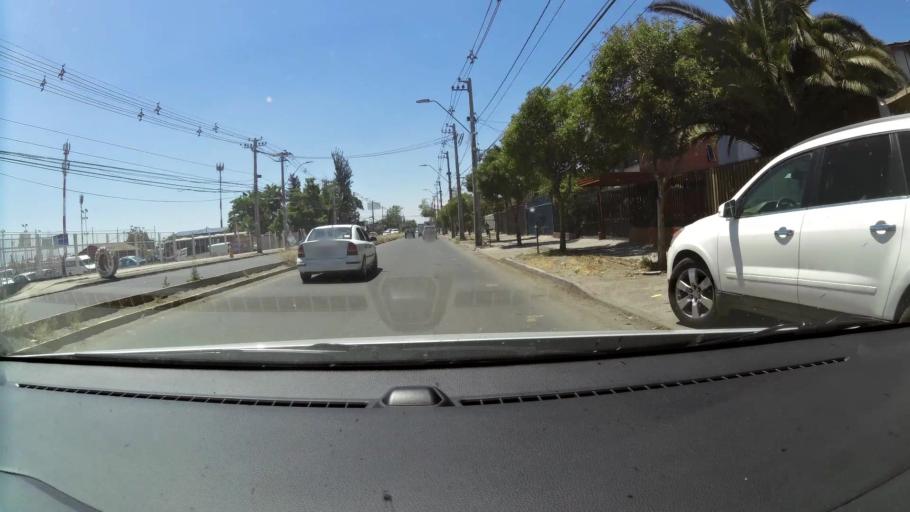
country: CL
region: Santiago Metropolitan
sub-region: Provincia de Maipo
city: San Bernardo
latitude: -33.6014
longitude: -70.6816
